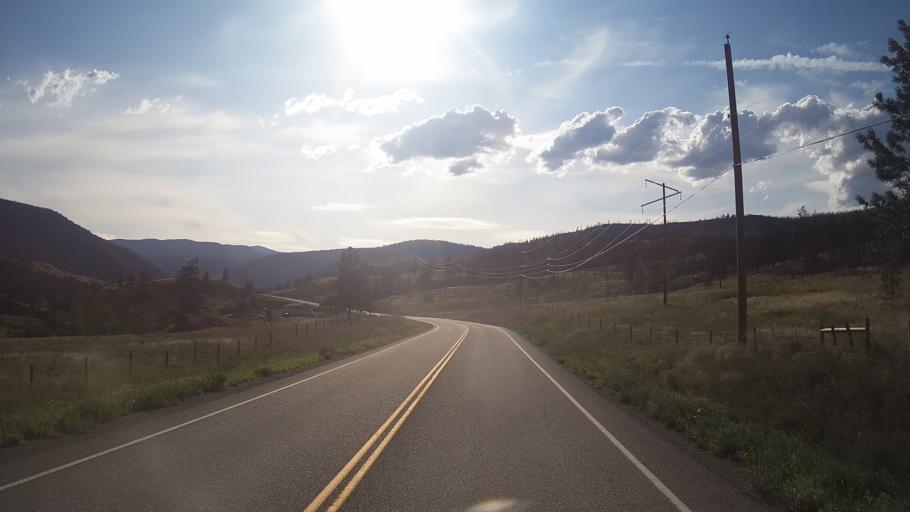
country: CA
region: British Columbia
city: Cache Creek
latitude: 50.8874
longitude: -121.4483
